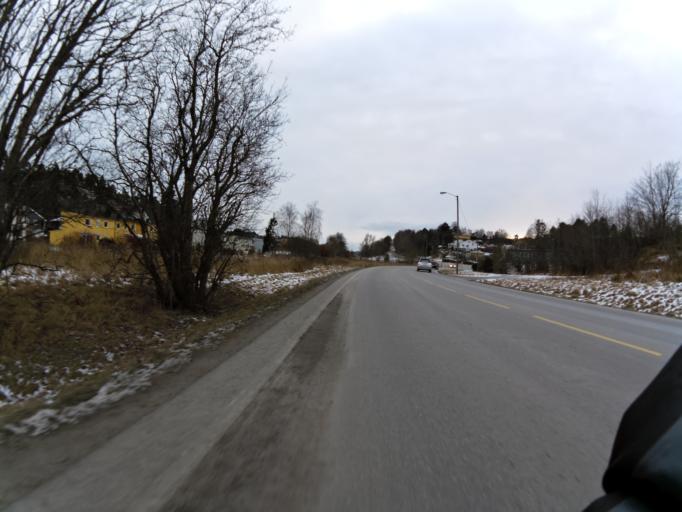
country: NO
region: Ostfold
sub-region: Fredrikstad
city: Fredrikstad
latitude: 59.2291
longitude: 10.9018
